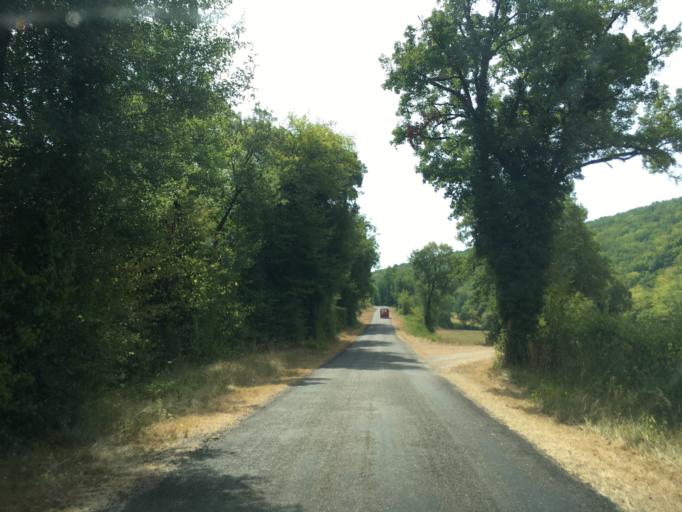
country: FR
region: Midi-Pyrenees
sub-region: Departement du Lot
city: Gramat
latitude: 44.7654
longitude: 1.5841
